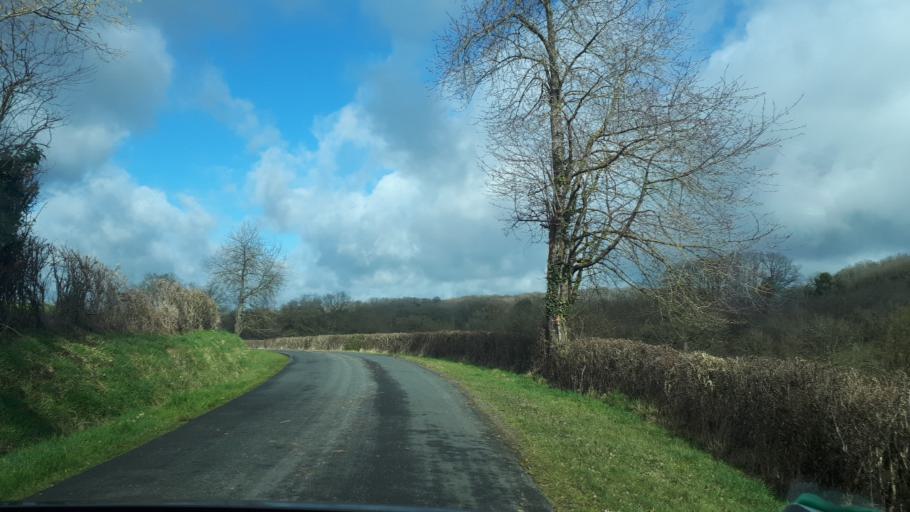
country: FR
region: Centre
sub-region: Departement du Loir-et-Cher
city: Sarge-sur-Braye
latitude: 47.9125
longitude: 0.8694
